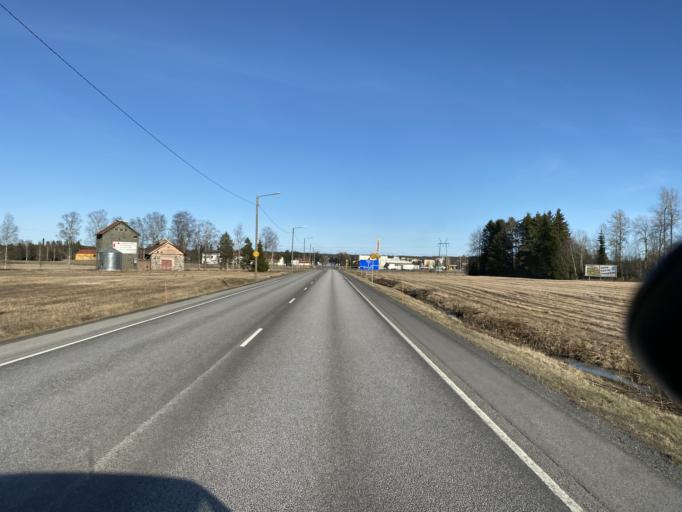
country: FI
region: Satakunta
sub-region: Rauma
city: Eura
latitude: 61.1313
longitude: 22.1176
